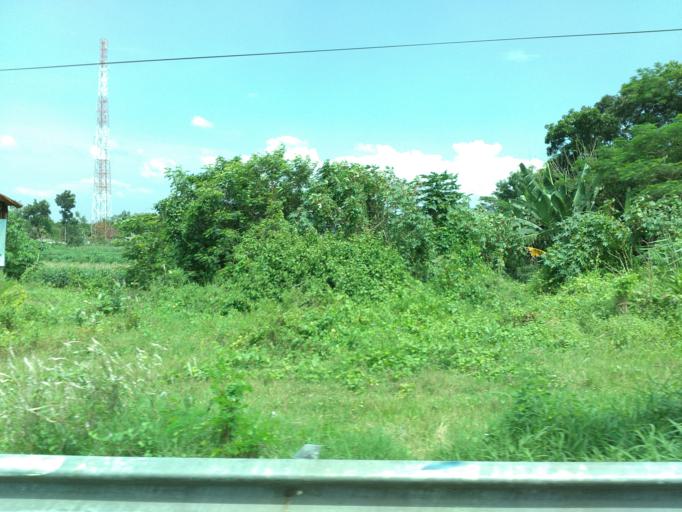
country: ID
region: Central Java
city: Candi Prambanan
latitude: -7.7426
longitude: 110.5302
